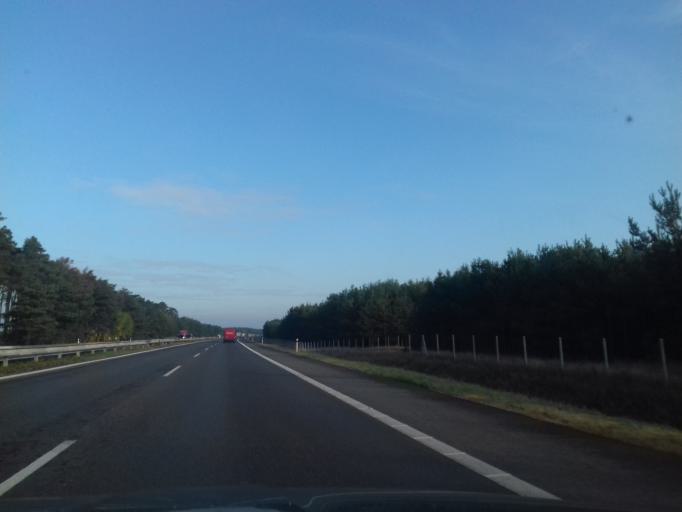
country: SK
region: Bratislavsky
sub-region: Okres Malacky
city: Malacky
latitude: 48.3800
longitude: 17.0215
